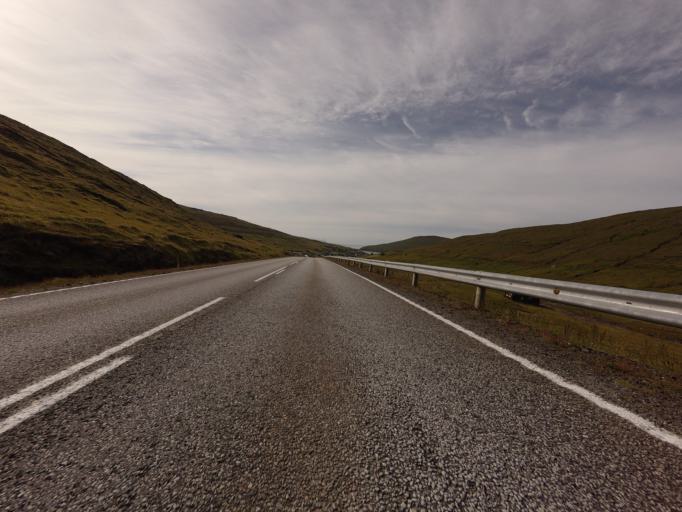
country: FO
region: Vagar
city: Midvagur
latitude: 62.0687
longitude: -7.1505
